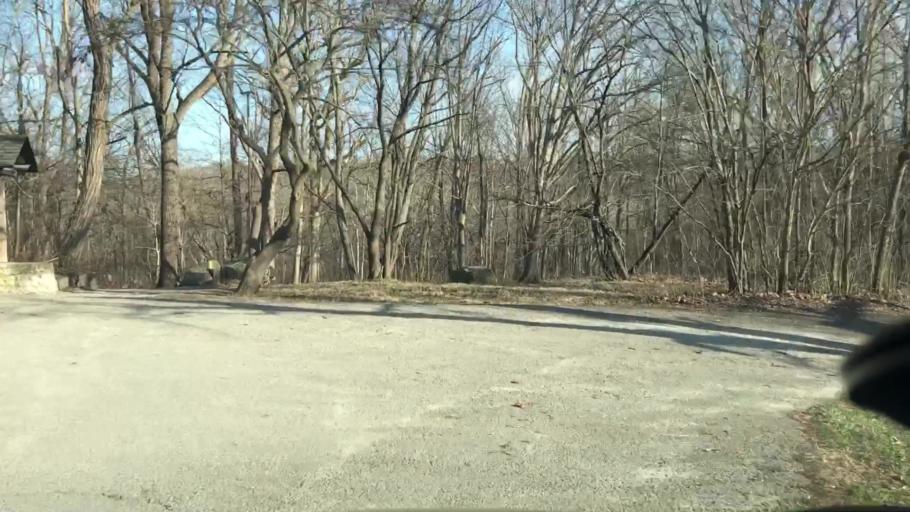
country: US
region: Ohio
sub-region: Greene County
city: Yellow Springs
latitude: 39.8006
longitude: -83.8856
